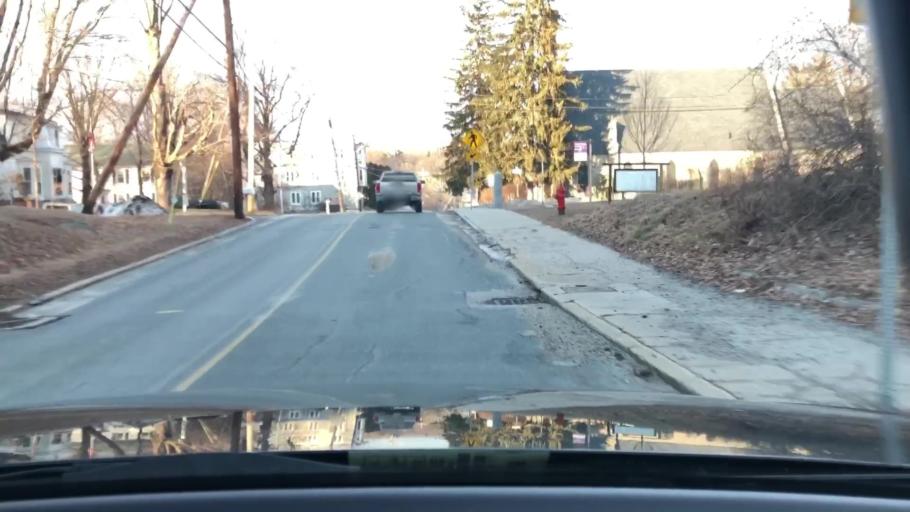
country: US
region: Massachusetts
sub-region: Worcester County
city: Millville
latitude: 42.0237
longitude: -71.5830
